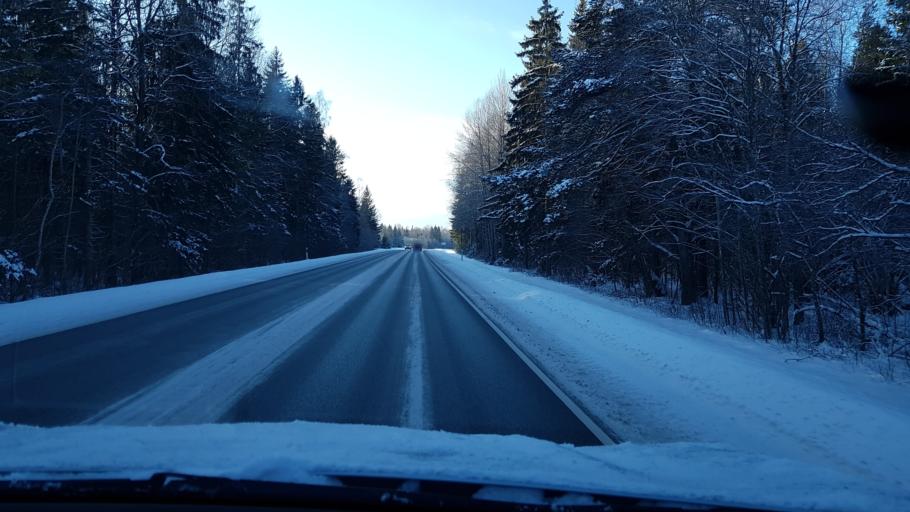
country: EE
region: Harju
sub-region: Nissi vald
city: Riisipere
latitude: 59.1813
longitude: 24.3823
